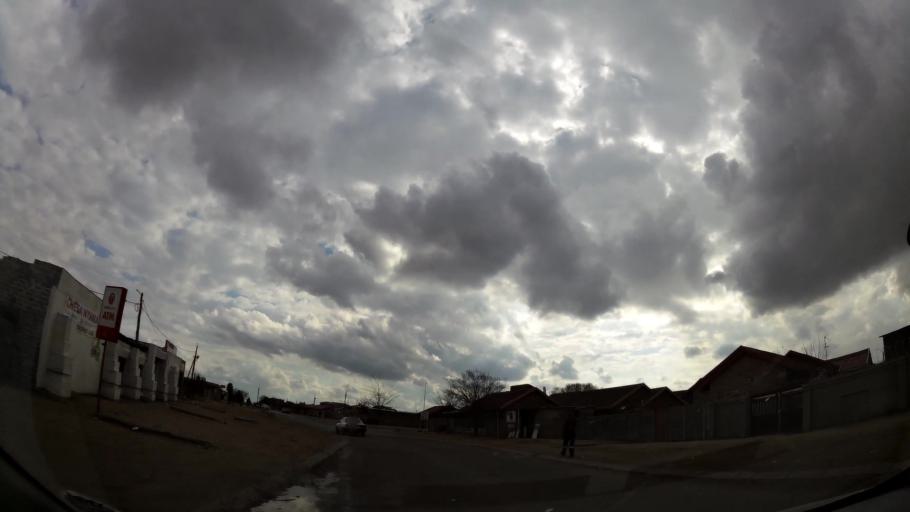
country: ZA
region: Orange Free State
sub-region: Fezile Dabi District Municipality
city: Sasolburg
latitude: -26.8497
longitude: 27.8595
